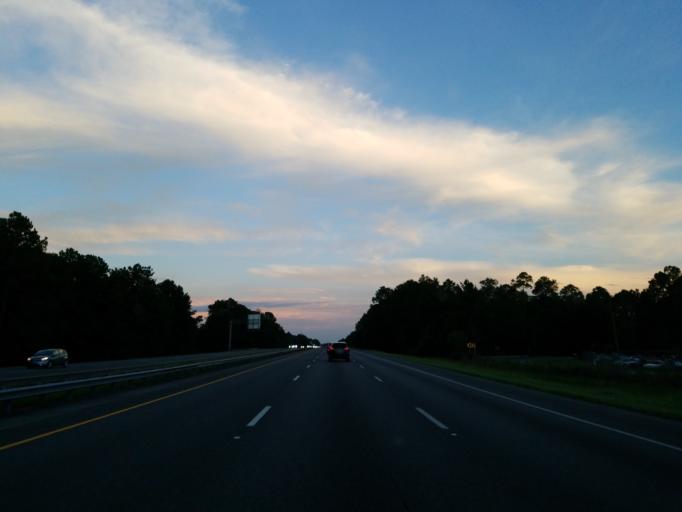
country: US
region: Georgia
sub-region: Lowndes County
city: Valdosta
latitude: 30.7377
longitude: -83.2658
